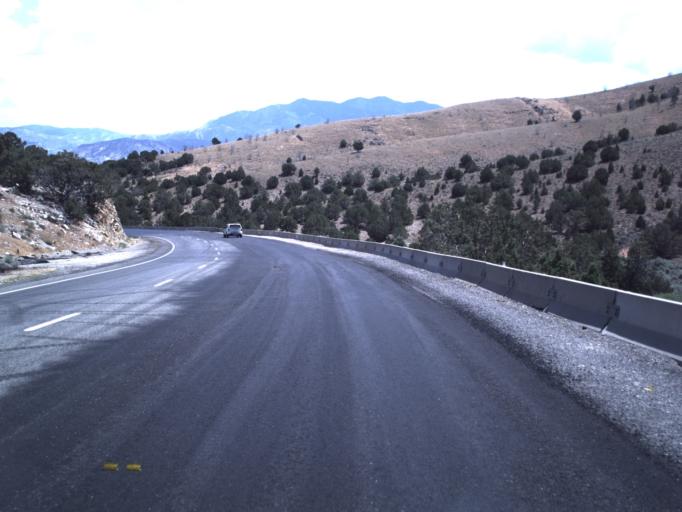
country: US
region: Utah
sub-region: Juab County
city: Nephi
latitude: 39.6976
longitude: -111.9427
